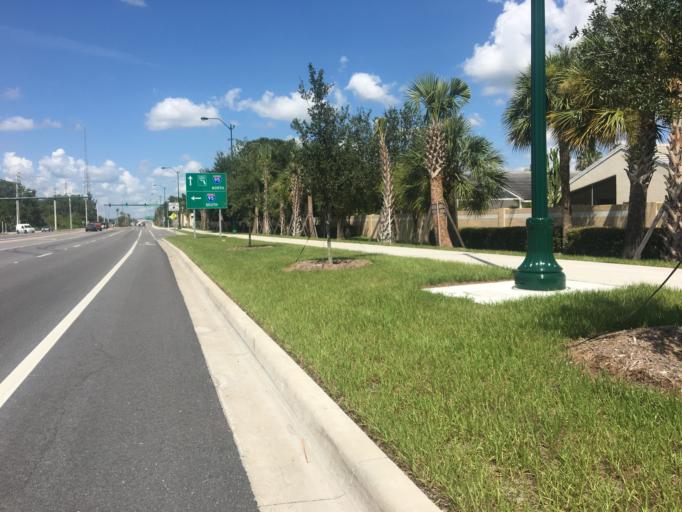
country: US
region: Florida
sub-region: Martin County
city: Palm City
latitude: 27.1614
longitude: -80.2949
